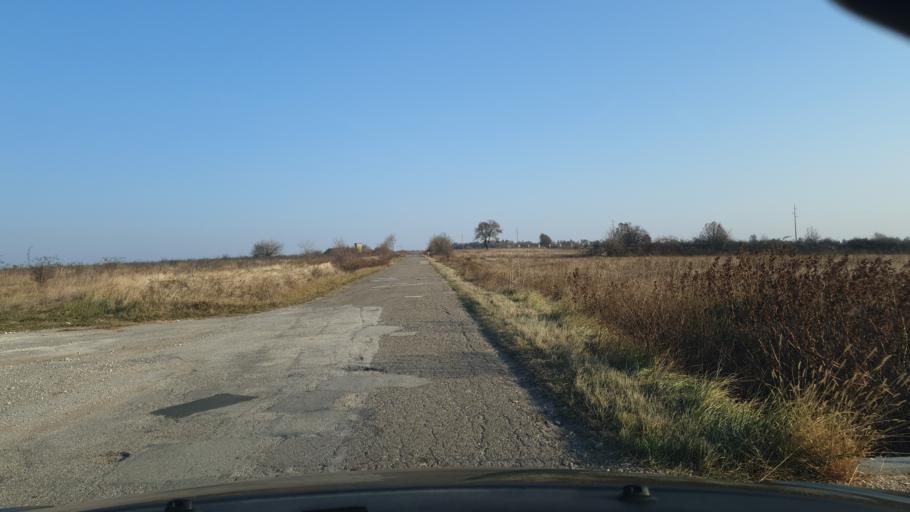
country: RS
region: Central Serbia
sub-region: Borski Okrug
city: Negotin
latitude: 44.1207
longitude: 22.3547
